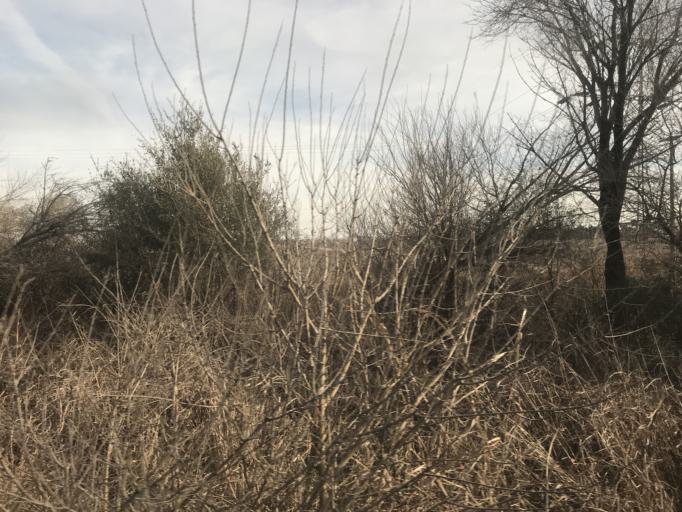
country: AR
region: Cordoba
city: Pilar
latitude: -31.7112
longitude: -63.8604
